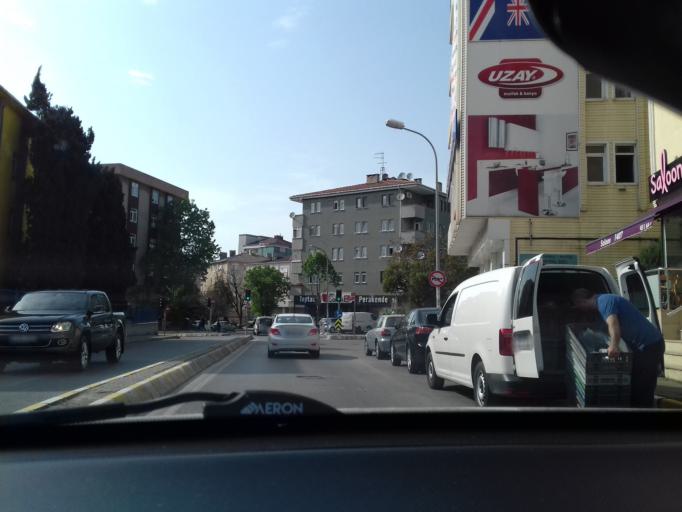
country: TR
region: Istanbul
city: Maltepe
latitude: 40.9155
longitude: 29.2071
